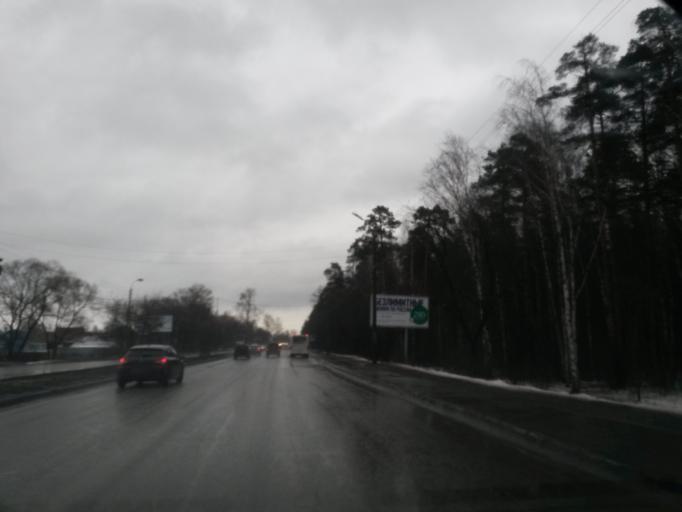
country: RU
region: Jaroslavl
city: Yaroslavl
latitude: 57.6469
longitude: 39.9235
